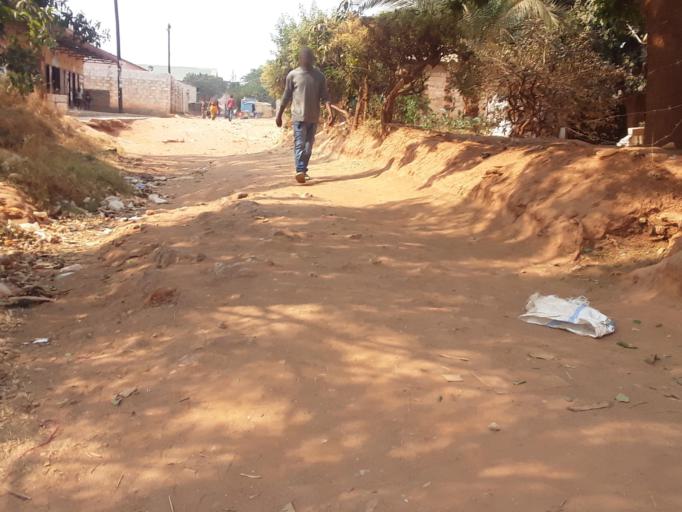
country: ZM
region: Lusaka
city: Lusaka
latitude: -15.3542
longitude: 28.2969
